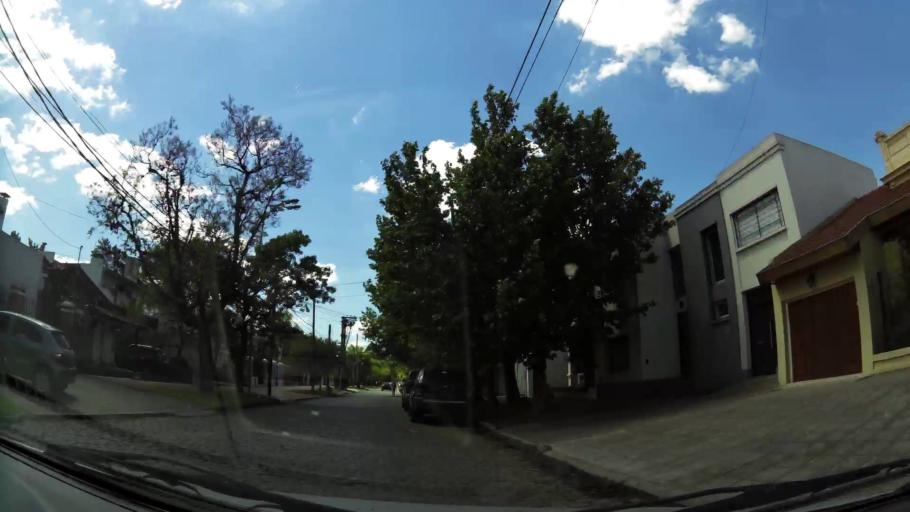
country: AR
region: Buenos Aires
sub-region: Partido de Lomas de Zamora
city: Lomas de Zamora
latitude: -34.7415
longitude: -58.4046
